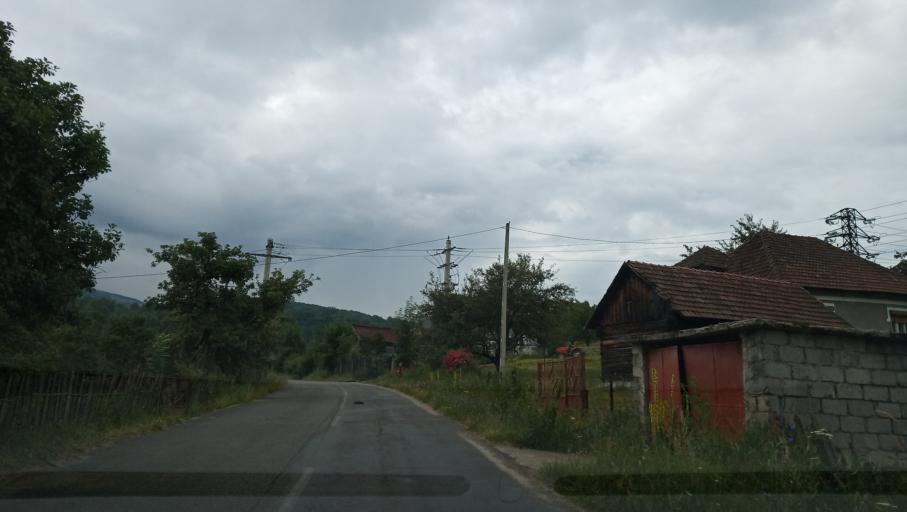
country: RO
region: Hunedoara
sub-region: Oras Petrila
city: Petrila
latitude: 45.4185
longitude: 23.4089
